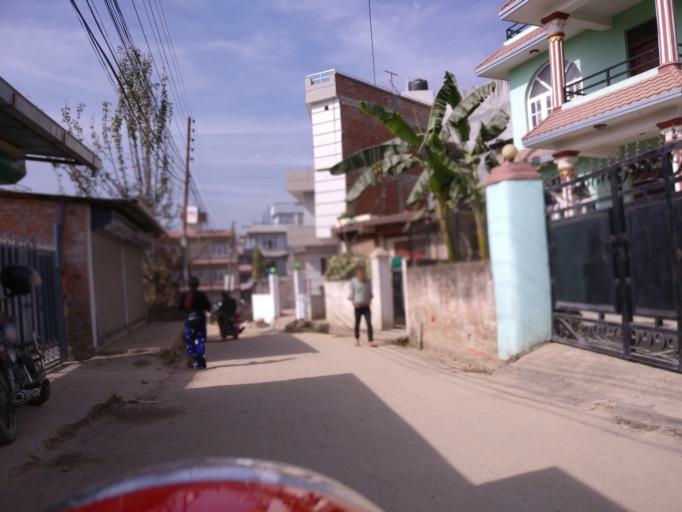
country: NP
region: Central Region
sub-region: Bagmati Zone
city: Patan
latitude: 27.6586
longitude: 85.3119
